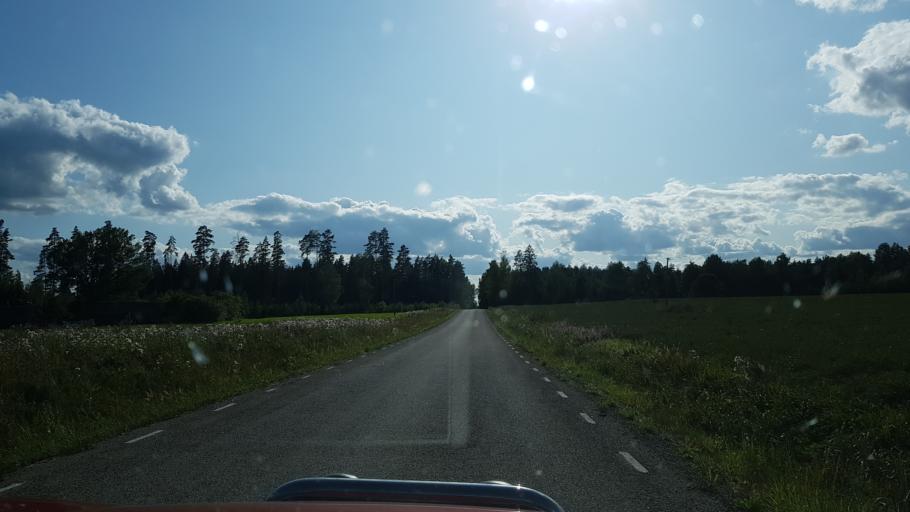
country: EE
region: Vorumaa
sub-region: Voru linn
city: Voru
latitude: 57.9254
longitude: 27.0441
